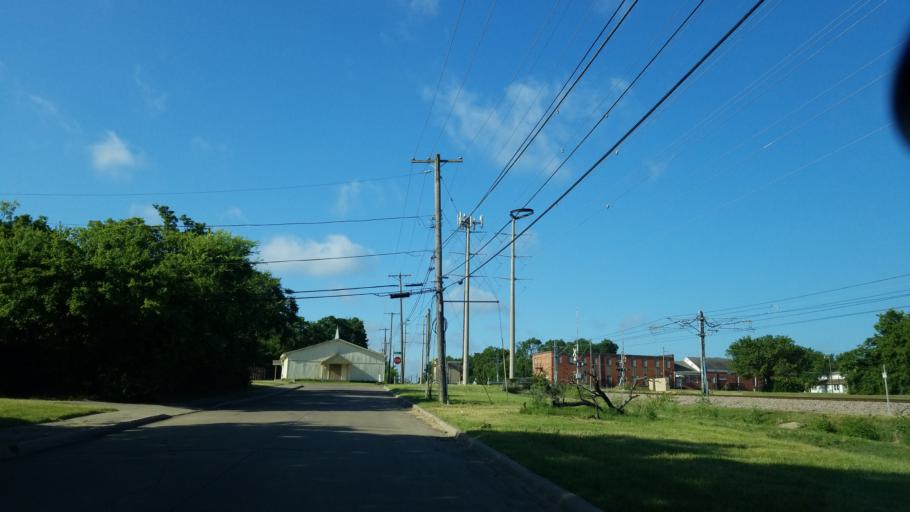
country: US
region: Texas
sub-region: Dallas County
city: Dallas
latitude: 32.7284
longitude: -96.8041
